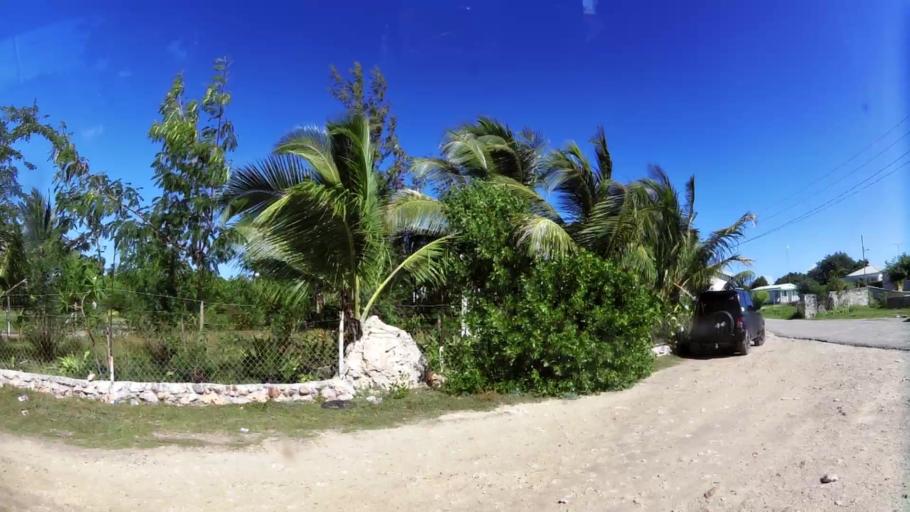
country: AG
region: Barbuda
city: Codrington
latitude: 17.6449
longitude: -61.8245
